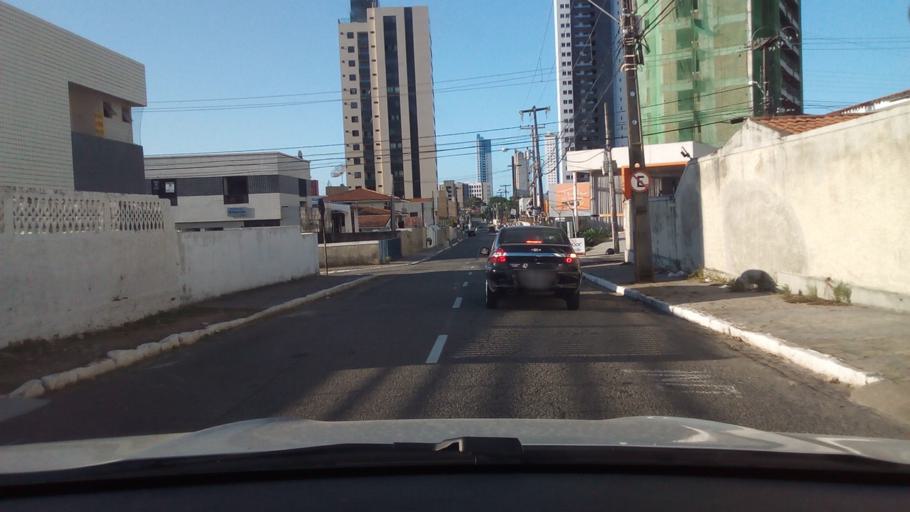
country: BR
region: Paraiba
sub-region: Joao Pessoa
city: Joao Pessoa
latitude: -7.1152
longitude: -34.8411
